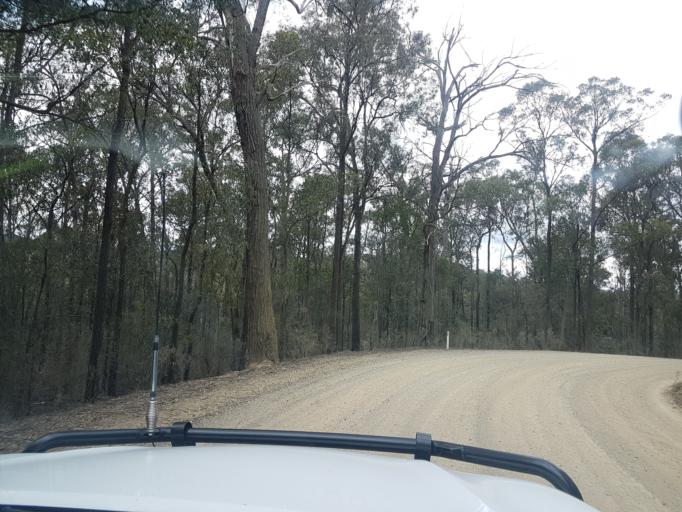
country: AU
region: Victoria
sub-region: East Gippsland
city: Bairnsdale
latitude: -37.6995
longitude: 147.5840
